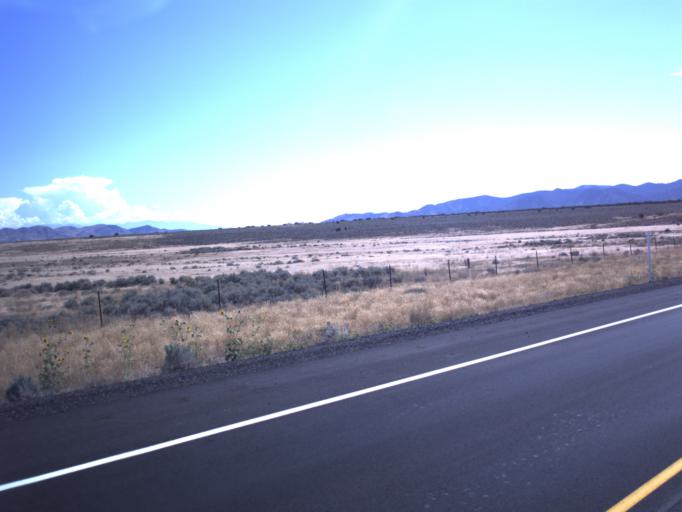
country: US
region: Utah
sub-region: Utah County
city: Eagle Mountain
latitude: 40.0747
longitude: -112.3395
